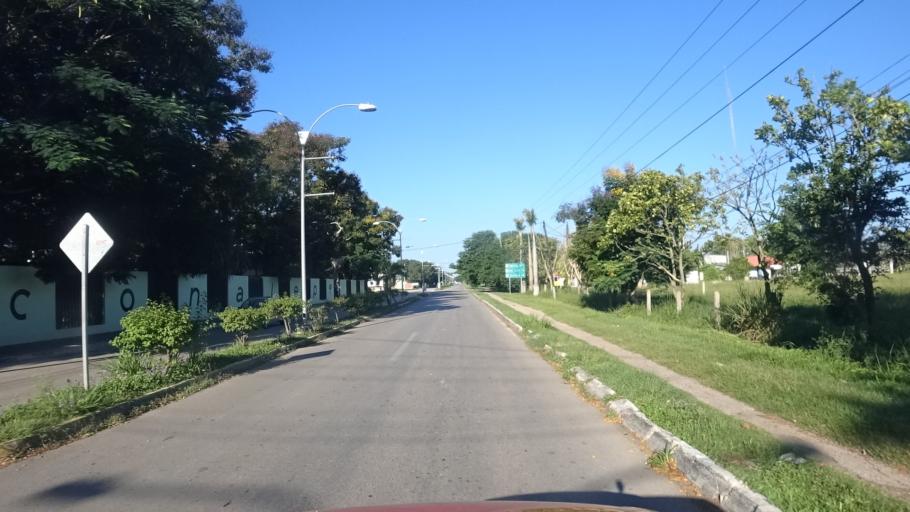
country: MX
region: Yucatan
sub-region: Tizimin
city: Tizimin
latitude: 21.1524
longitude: -88.1730
